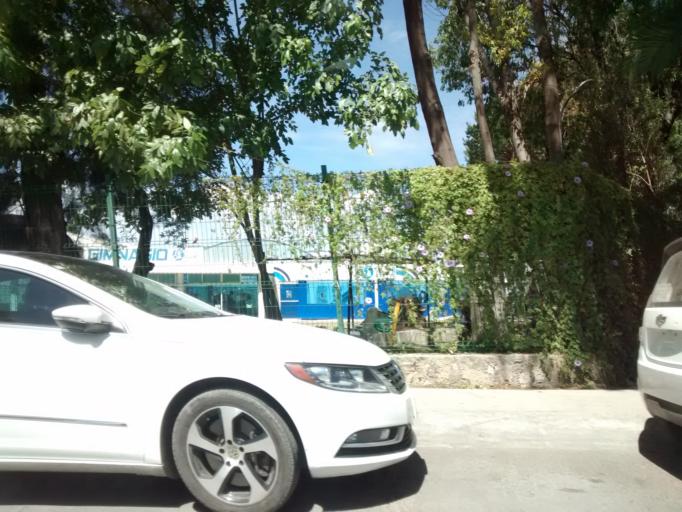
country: MX
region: Puebla
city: Tehuacan
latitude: 18.4694
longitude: -97.4147
